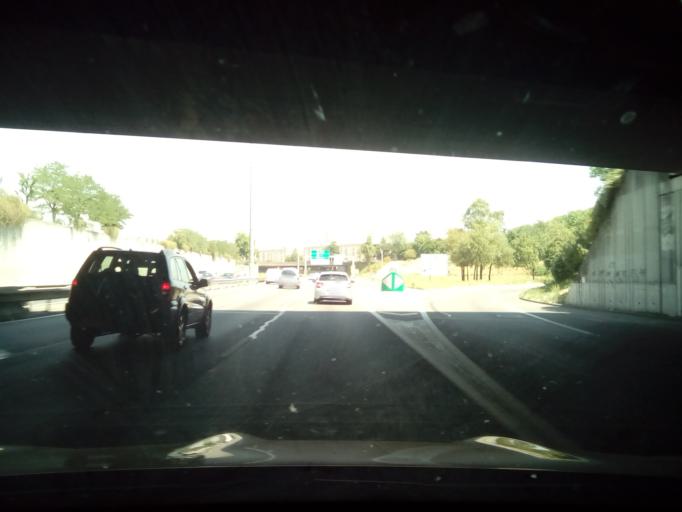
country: FR
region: Rhone-Alpes
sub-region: Departement du Rhone
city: Bron
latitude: 45.7581
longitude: 4.9092
